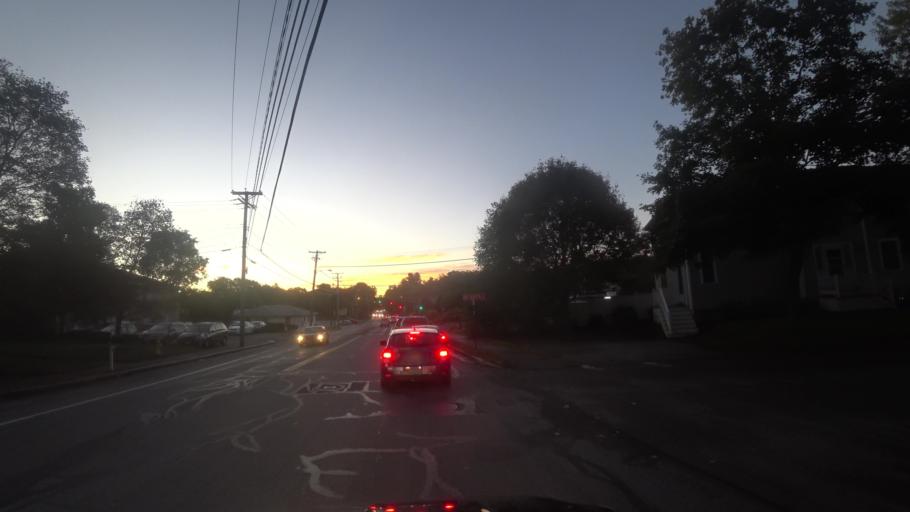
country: US
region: Massachusetts
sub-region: Essex County
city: Saugus
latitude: 42.4733
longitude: -71.0373
